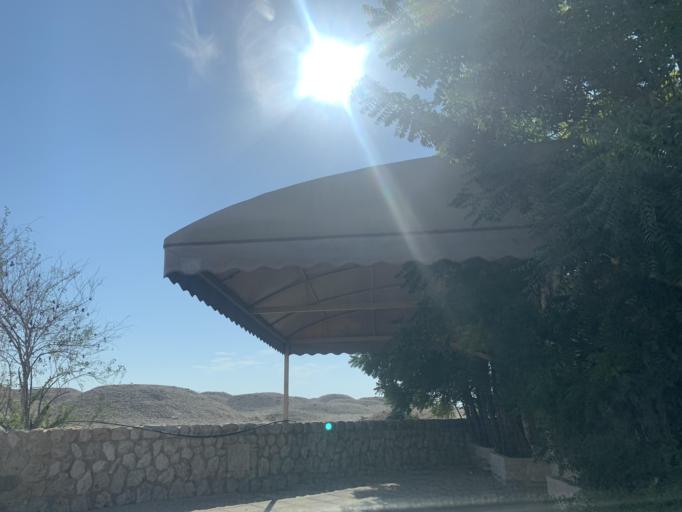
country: BH
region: Central Governorate
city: Madinat Hamad
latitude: 26.1274
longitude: 50.4975
